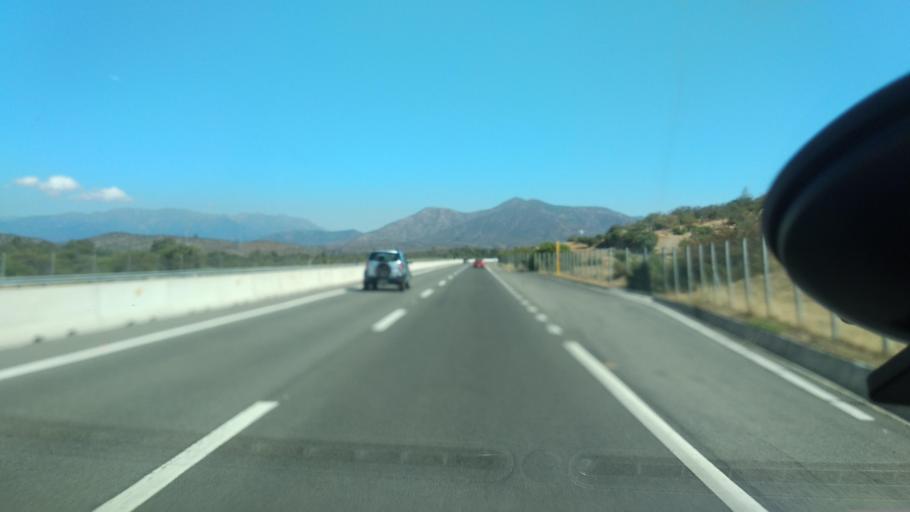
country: CL
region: Valparaiso
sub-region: Provincia de Marga Marga
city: Limache
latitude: -33.0130
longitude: -71.3226
